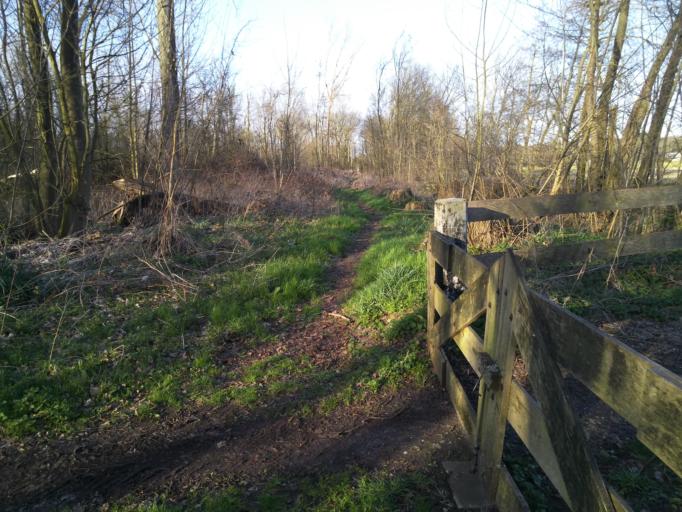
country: NL
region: South Holland
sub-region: Gemeente Lisse
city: Lisse
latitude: 52.2581
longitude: 4.5301
